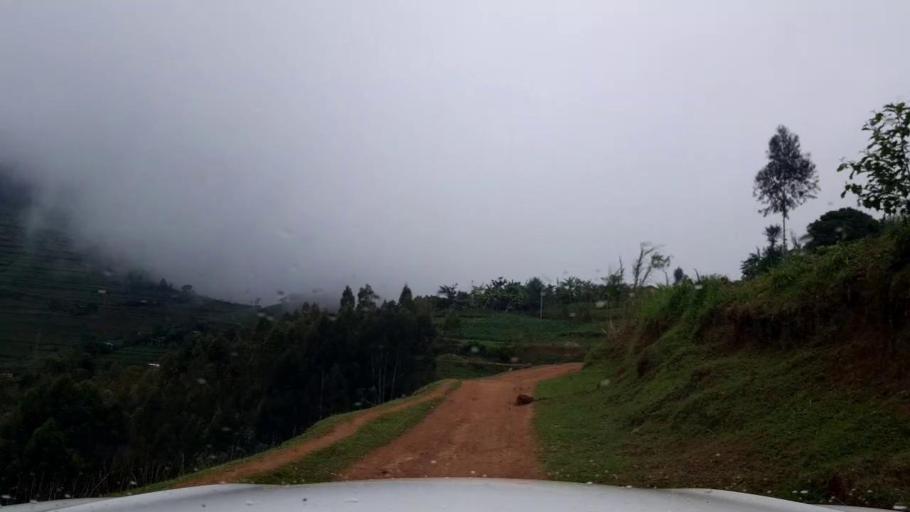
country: RW
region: Northern Province
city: Musanze
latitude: -1.5956
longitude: 29.7901
